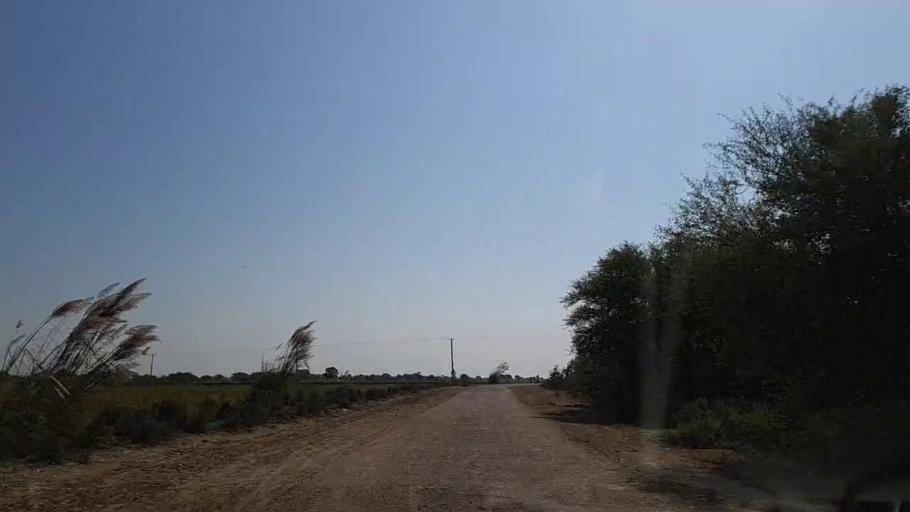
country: PK
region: Sindh
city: Chuhar Jamali
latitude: 24.5221
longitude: 68.0923
